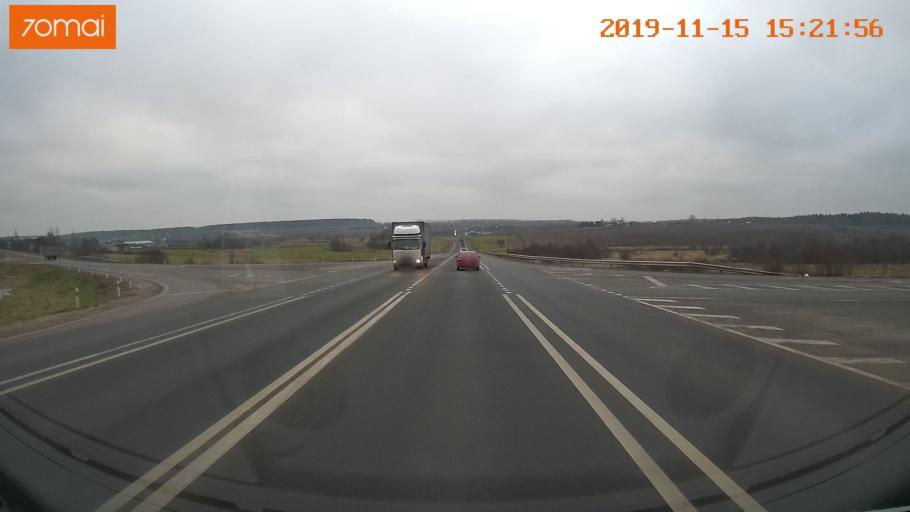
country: RU
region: Jaroslavl
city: Danilov
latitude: 58.2081
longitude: 40.1391
